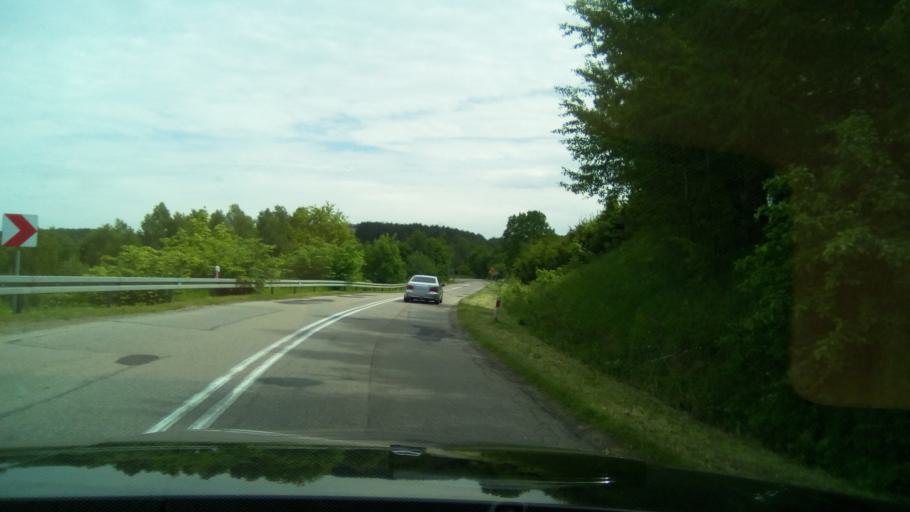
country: PL
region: Pomeranian Voivodeship
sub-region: Powiat bytowski
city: Lipnica
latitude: 54.0867
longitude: 17.4416
